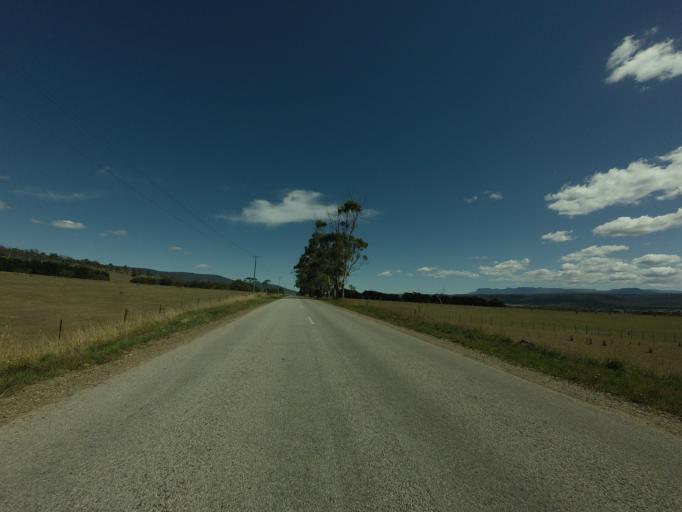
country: AU
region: Tasmania
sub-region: Break O'Day
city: St Helens
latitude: -41.6158
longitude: 148.0101
